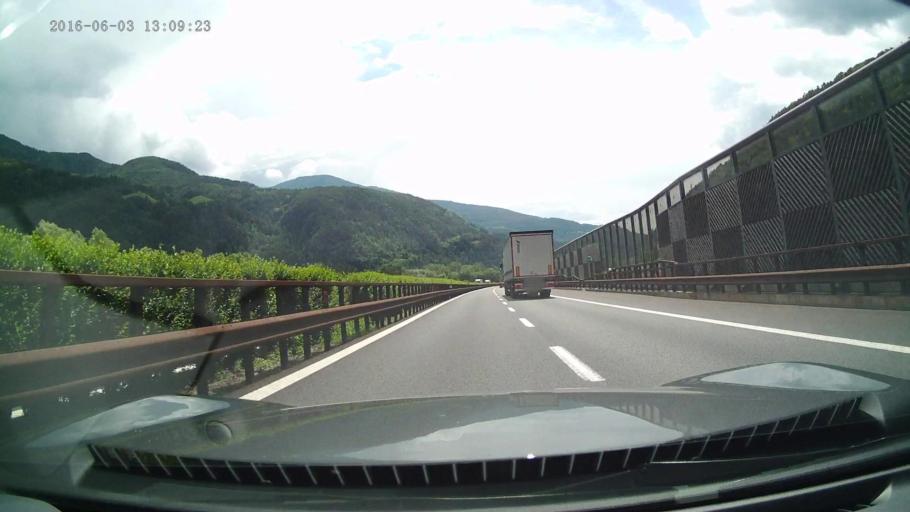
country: IT
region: Trentino-Alto Adige
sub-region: Bolzano
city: Velturno
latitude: 46.6776
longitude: 11.6220
